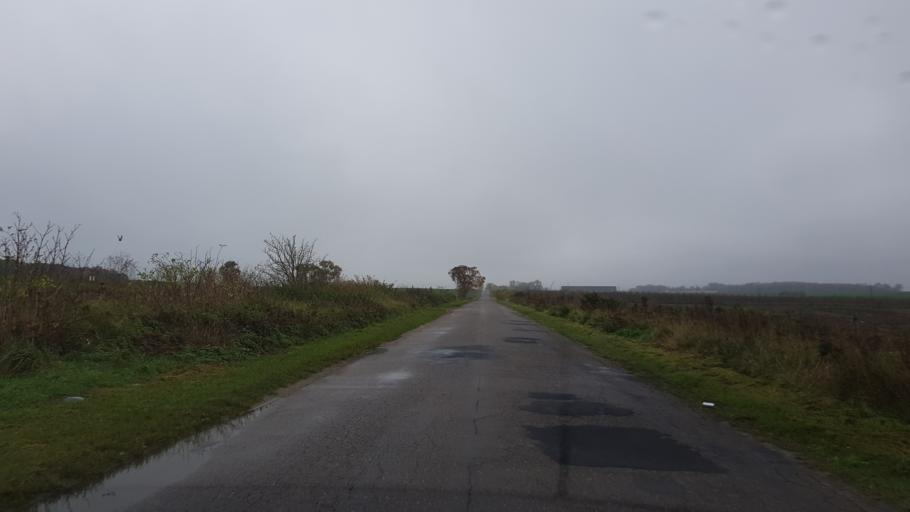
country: PL
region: West Pomeranian Voivodeship
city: Trzcinsko Zdroj
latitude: 53.0751
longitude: 14.5303
